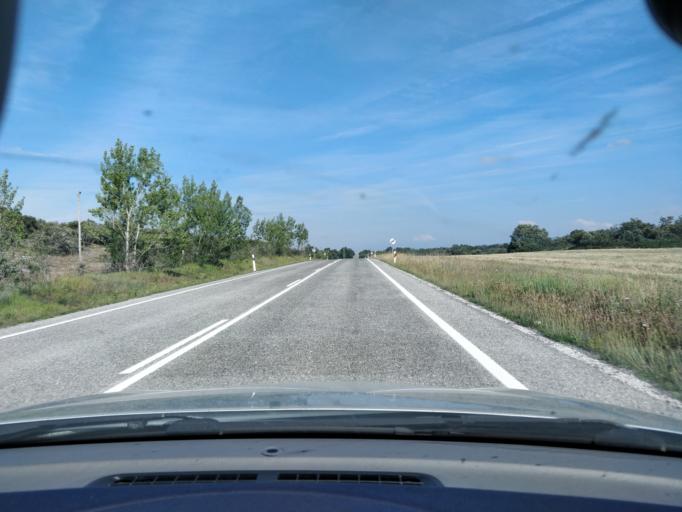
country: ES
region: Cantabria
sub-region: Provincia de Cantabria
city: San Martin de Elines
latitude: 42.9434
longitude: -3.7462
